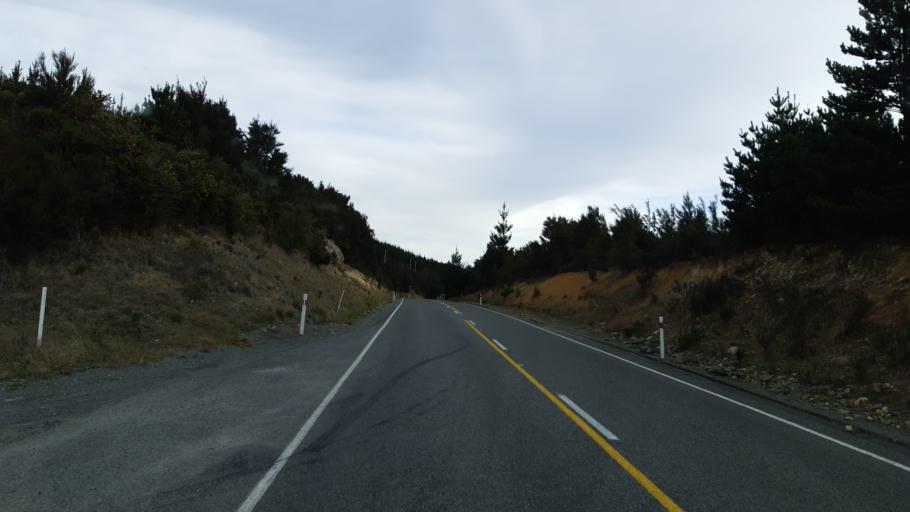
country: NZ
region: Tasman
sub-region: Tasman District
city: Brightwater
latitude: -41.6610
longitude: 173.2213
